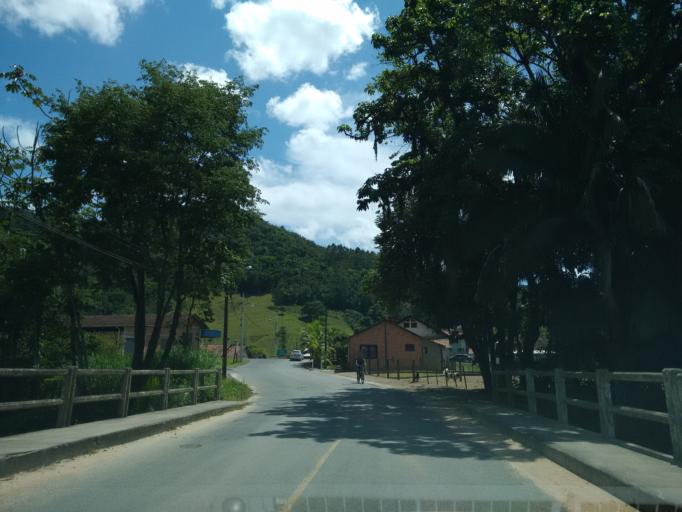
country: BR
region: Santa Catarina
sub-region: Pomerode
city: Pomerode
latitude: -26.7796
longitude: -49.1664
